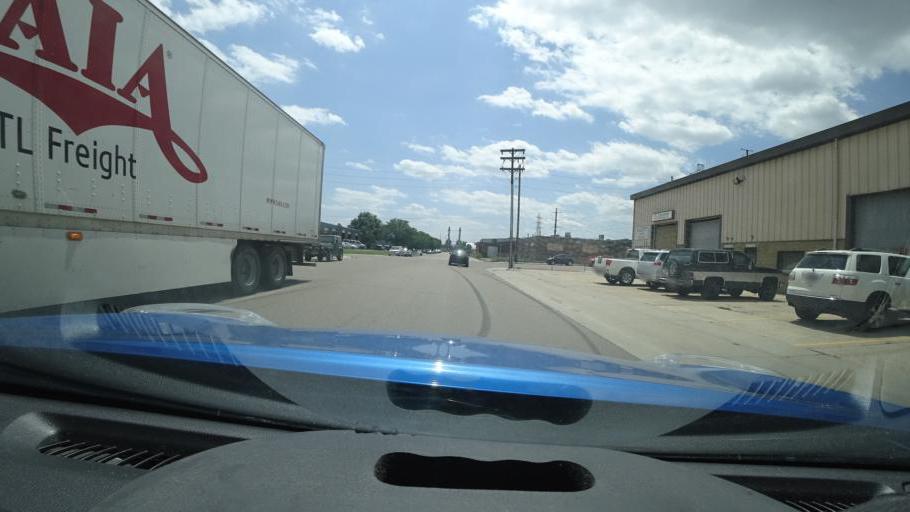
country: US
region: Colorado
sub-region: Arapahoe County
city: Englewood
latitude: 39.6753
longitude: -105.0018
